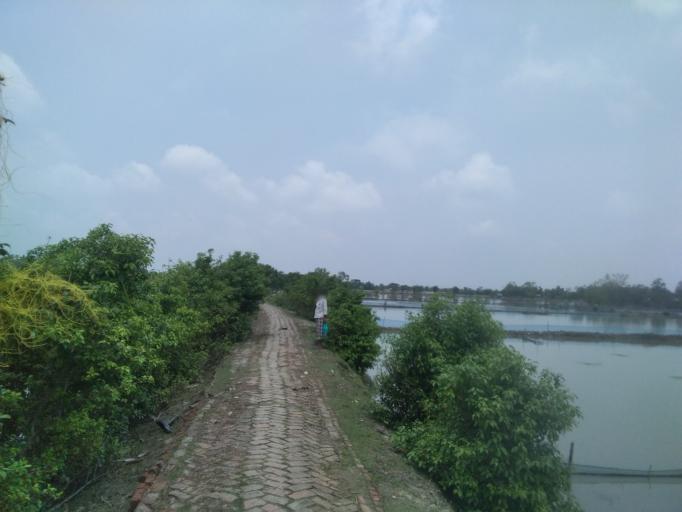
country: BD
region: Khulna
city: Phultala
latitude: 22.6394
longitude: 89.4055
